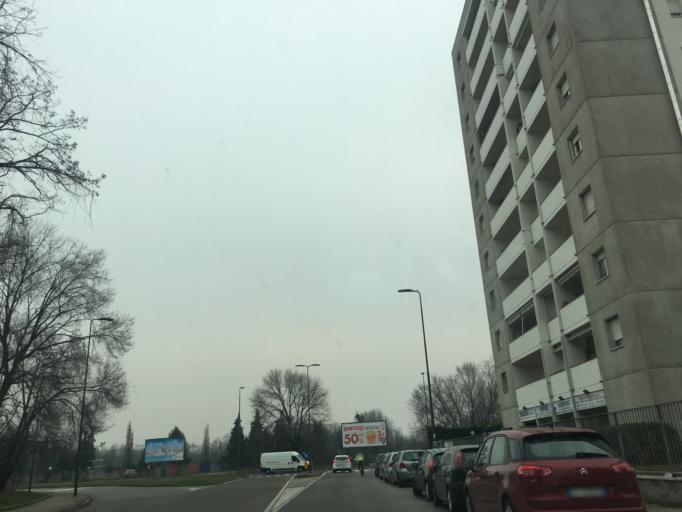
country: IT
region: Lombardy
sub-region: Citta metropolitana di Milano
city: Figino
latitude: 45.4766
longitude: 9.0936
